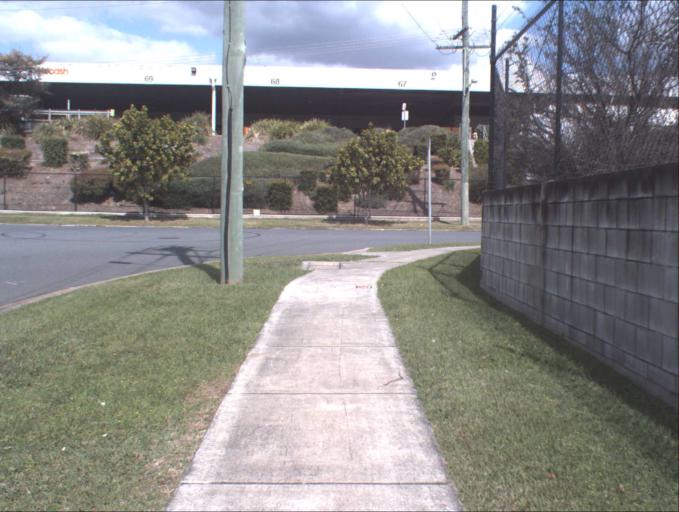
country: AU
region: Queensland
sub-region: Logan
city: Logan Reserve
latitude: -27.6876
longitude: 153.0751
